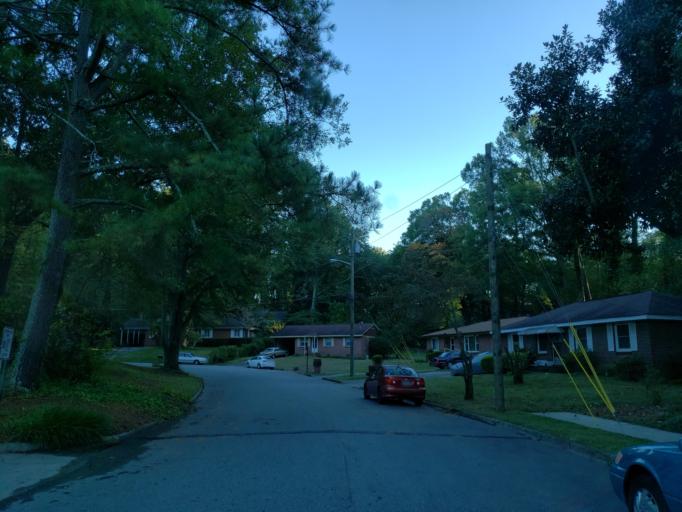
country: US
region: Georgia
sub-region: Cobb County
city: Marietta
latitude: 33.9459
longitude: -84.5556
